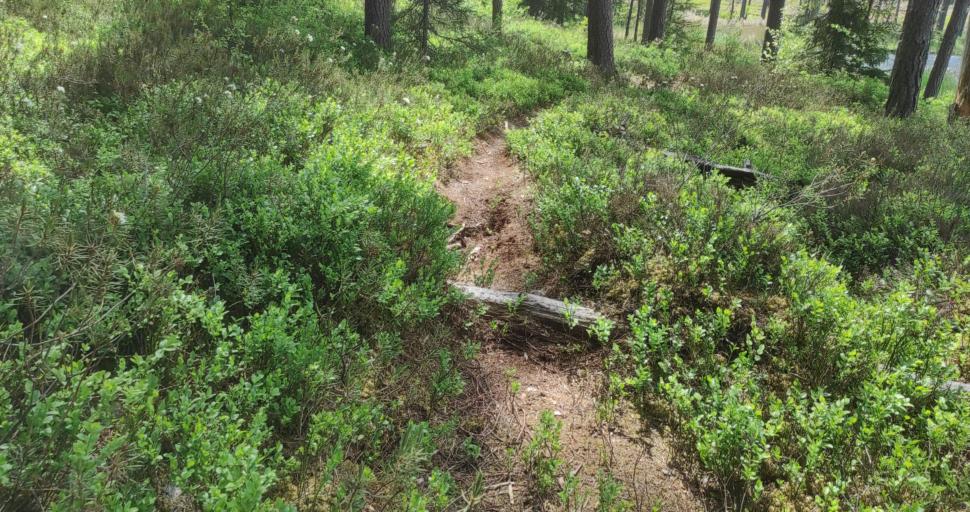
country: LV
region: Talsu Rajons
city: Stende
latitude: 57.1246
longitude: 22.3449
